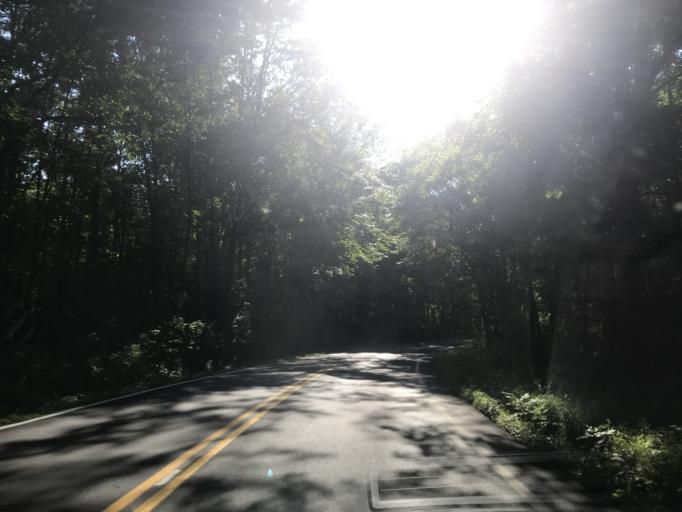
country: US
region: Maryland
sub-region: Harford County
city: Aberdeen
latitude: 39.5183
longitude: -76.1331
